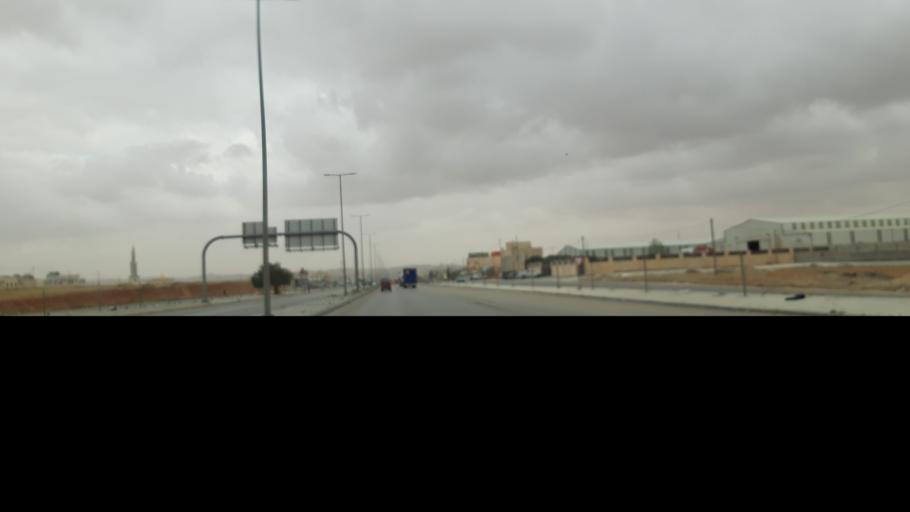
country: JO
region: Amman
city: Sahab
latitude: 31.8447
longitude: 36.0439
